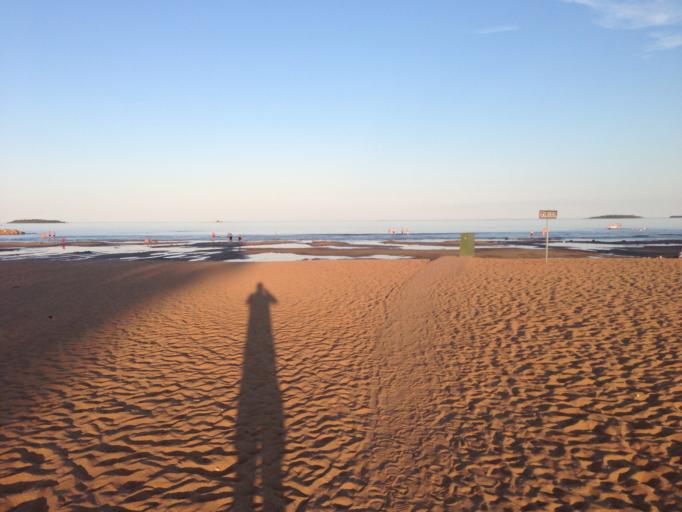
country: SE
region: Vaesterbotten
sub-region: Skelleftea Kommun
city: Byske
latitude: 64.9470
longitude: 21.2386
